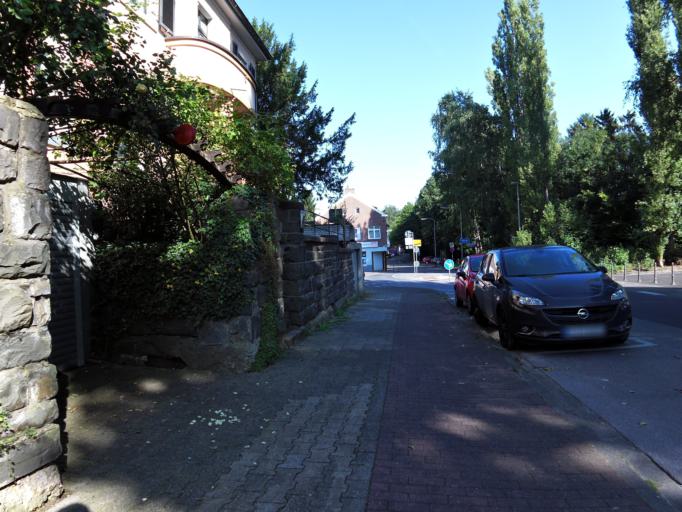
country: DE
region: North Rhine-Westphalia
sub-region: Regierungsbezirk Koln
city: Herzogenrath
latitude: 50.8718
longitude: 6.0883
